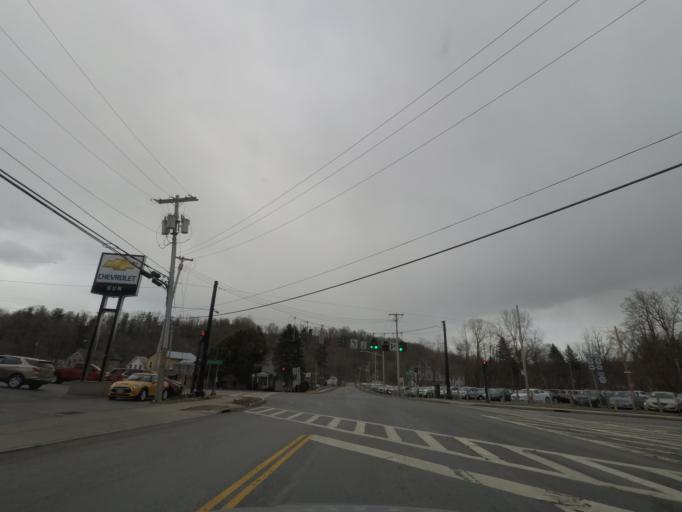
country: US
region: New York
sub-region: Madison County
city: Chittenango
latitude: 43.0425
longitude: -75.8691
